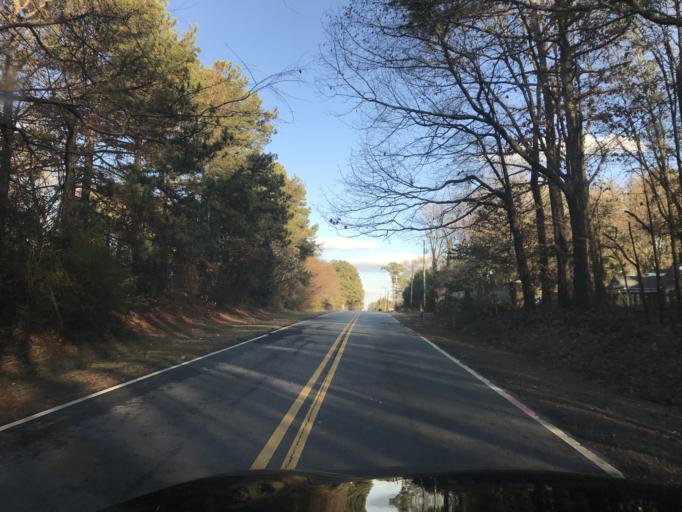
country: US
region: Georgia
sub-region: Fulton County
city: College Park
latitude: 33.6230
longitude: -84.4842
